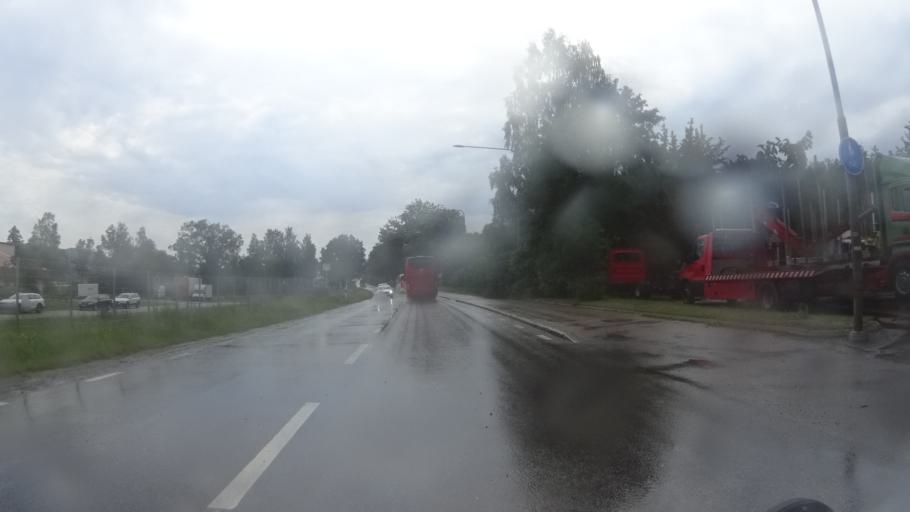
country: SE
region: OEstergoetland
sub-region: Kinda Kommun
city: Kisa
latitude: 57.9978
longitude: 15.6408
